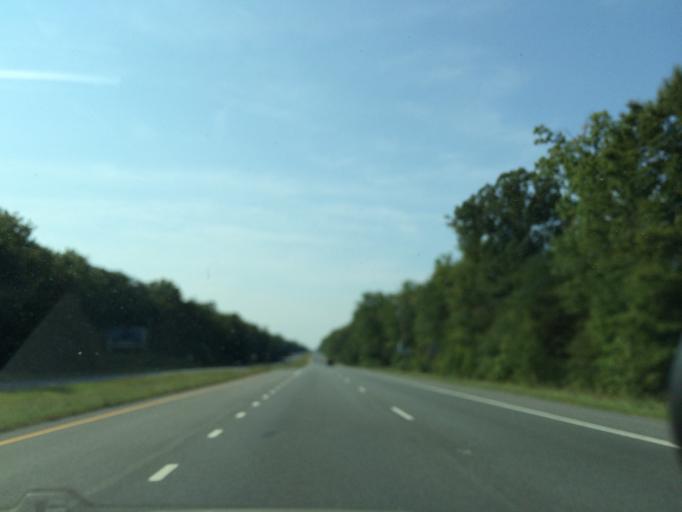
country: US
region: Maryland
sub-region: Charles County
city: La Plata
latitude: 38.4926
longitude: -76.9873
